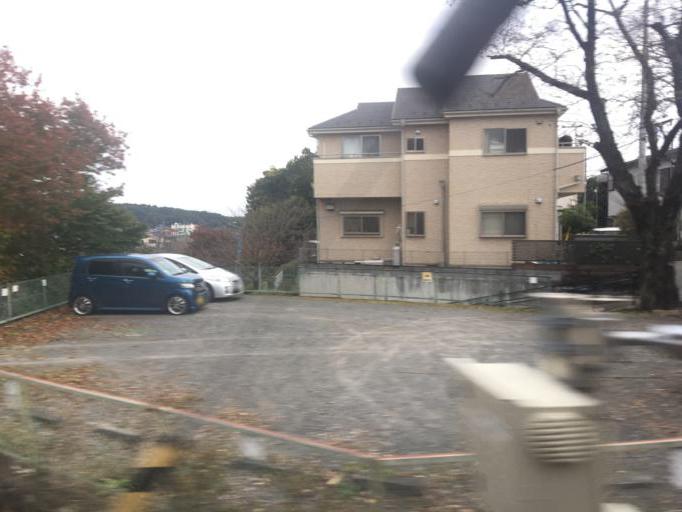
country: JP
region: Saitama
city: Hanno
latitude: 35.8126
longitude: 139.3278
